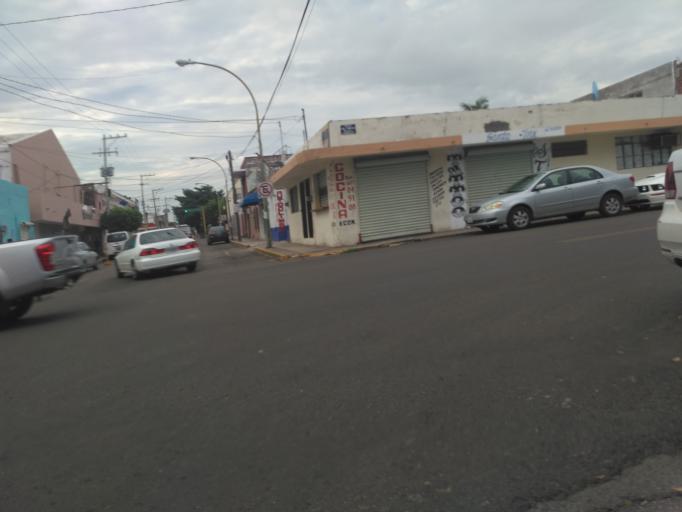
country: MX
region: Sinaloa
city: Culiacan
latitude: 24.8035
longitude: -107.3978
